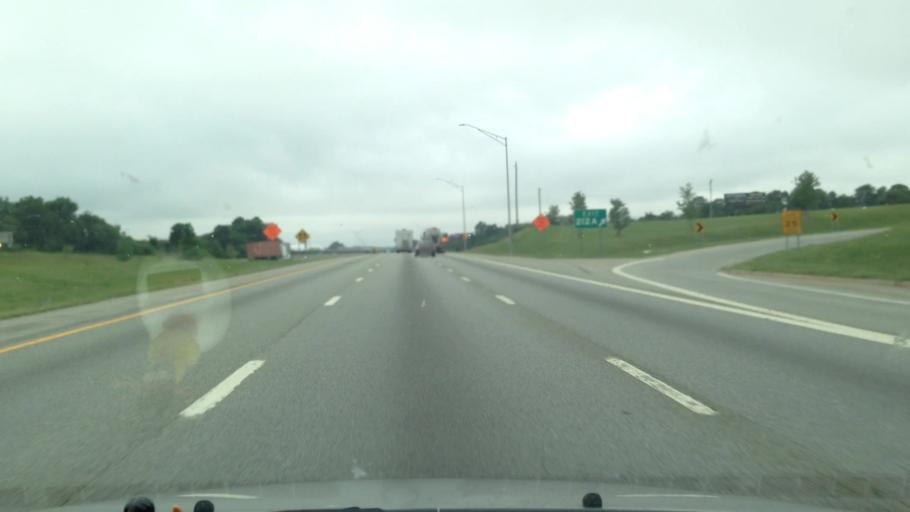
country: US
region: North Carolina
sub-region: Guilford County
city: Jamestown
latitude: 36.0675
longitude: -79.9208
